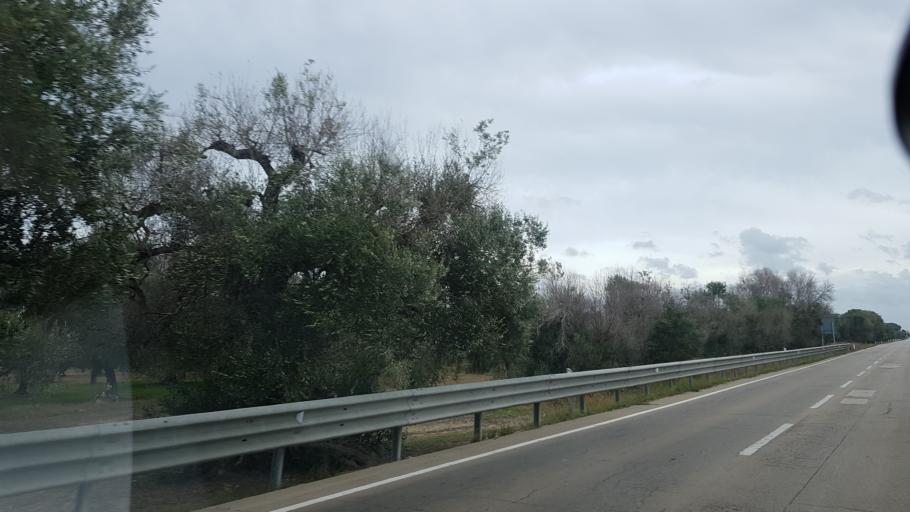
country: IT
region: Apulia
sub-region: Provincia di Lecce
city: Guagnano
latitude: 40.3990
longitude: 17.9295
